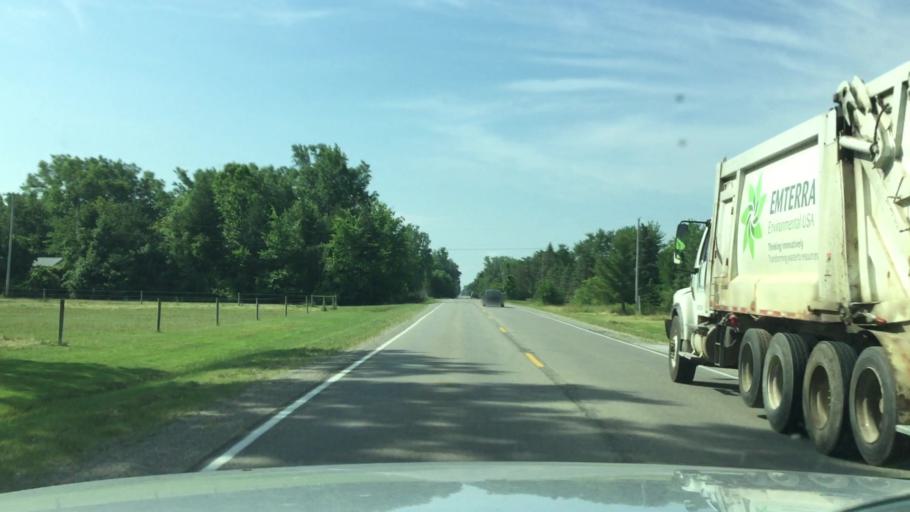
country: US
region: Michigan
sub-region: Genesee County
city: Flushing
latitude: 43.1253
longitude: -83.8138
